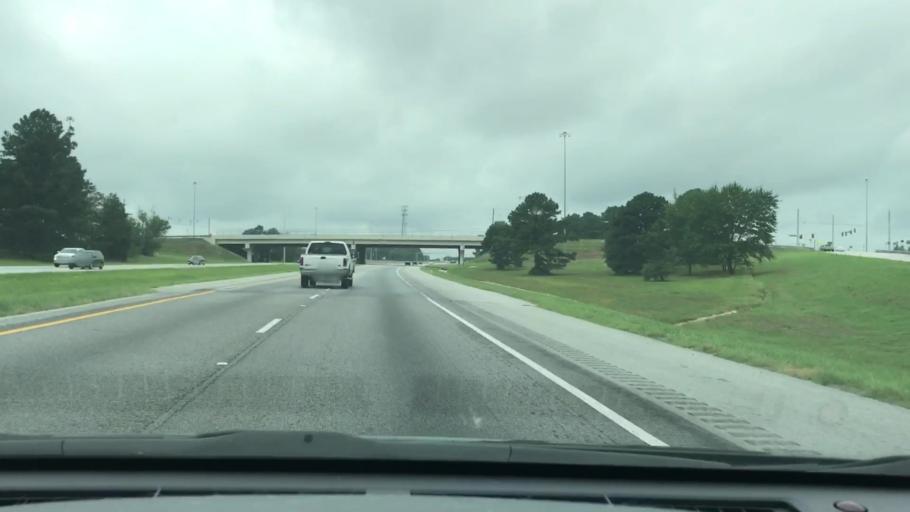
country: US
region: Georgia
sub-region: Newton County
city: Covington
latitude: 33.6123
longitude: -83.8219
